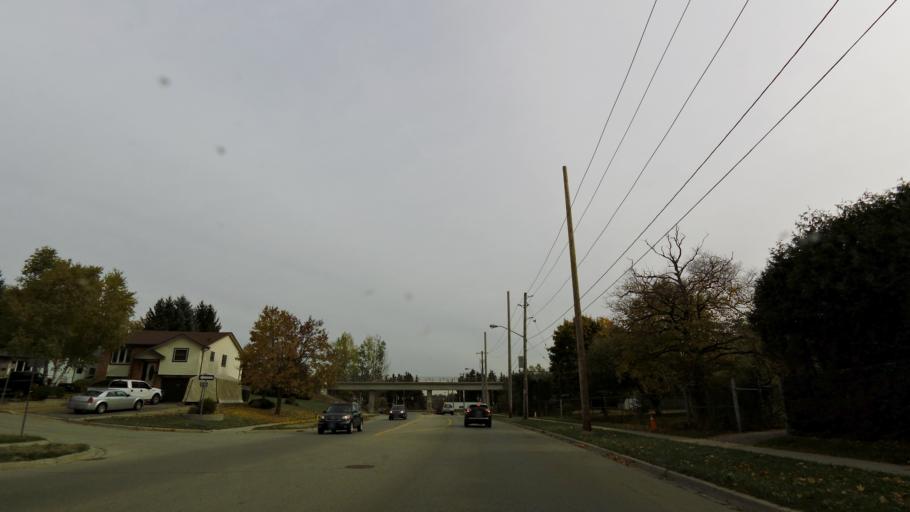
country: CA
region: Ontario
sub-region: Wellington County
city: Guelph
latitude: 43.5210
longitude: -80.2710
